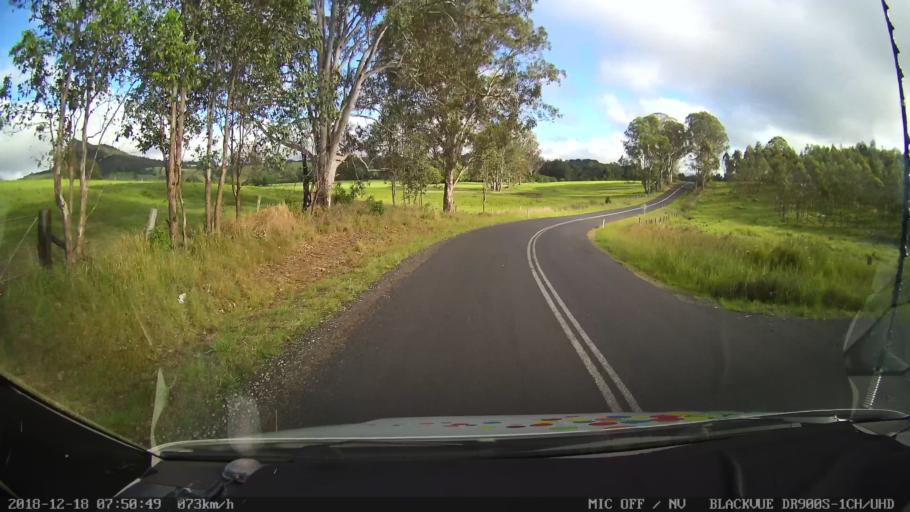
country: AU
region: New South Wales
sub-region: Kyogle
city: Kyogle
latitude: -28.4420
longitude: 152.5743
